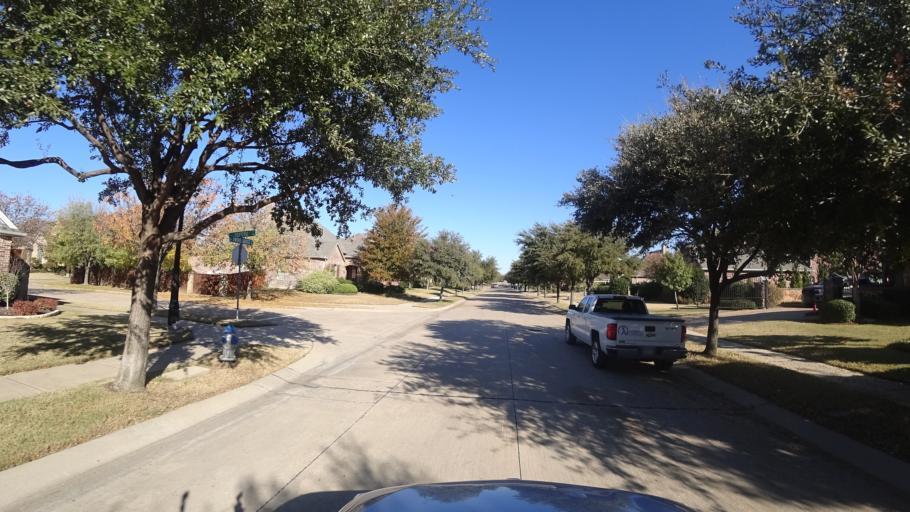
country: US
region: Texas
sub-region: Denton County
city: The Colony
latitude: 33.0371
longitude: -96.9128
